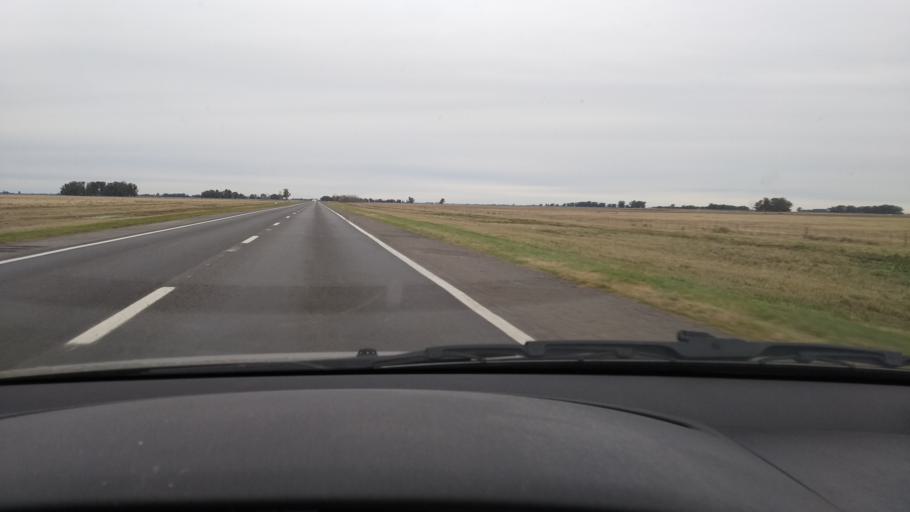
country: AR
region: Buenos Aires
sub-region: Partido de Las Flores
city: Las Flores
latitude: -36.1569
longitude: -59.2178
